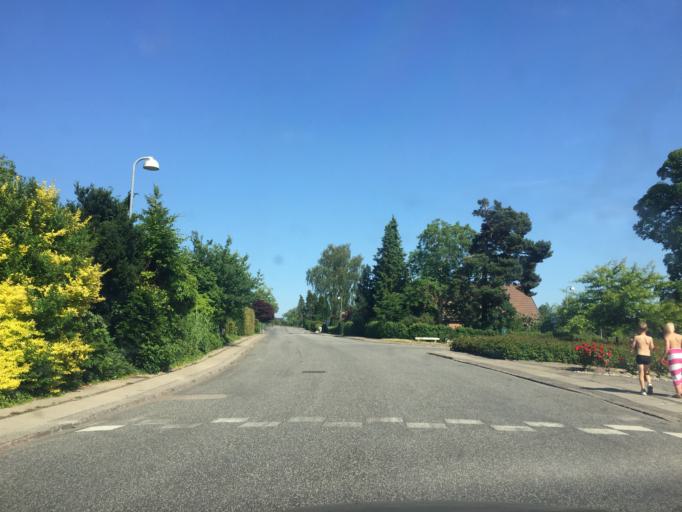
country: DK
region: Capital Region
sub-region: Fureso Kommune
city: Vaerlose
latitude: 55.7788
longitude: 12.3602
